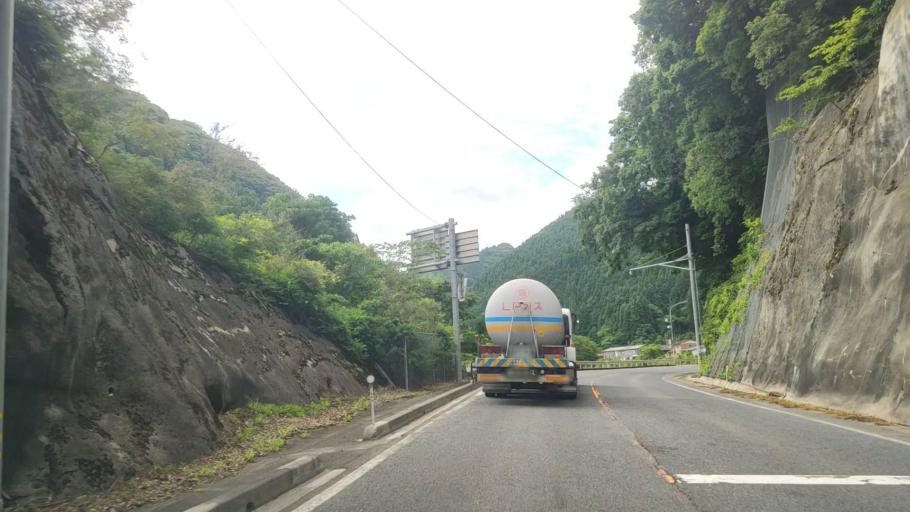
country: JP
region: Tottori
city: Yonago
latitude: 35.2357
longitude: 133.4395
